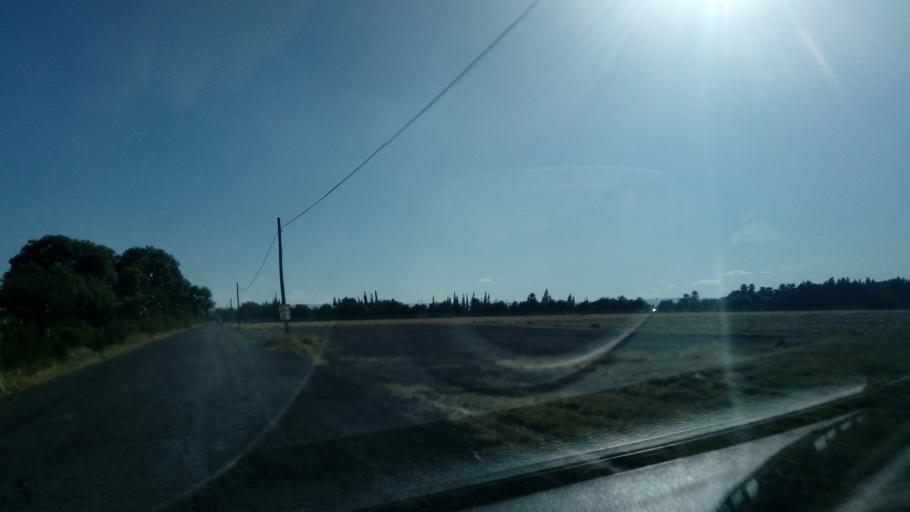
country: MX
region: Durango
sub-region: Durango
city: Jose Refugio Salcido
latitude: 24.0074
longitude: -104.5498
